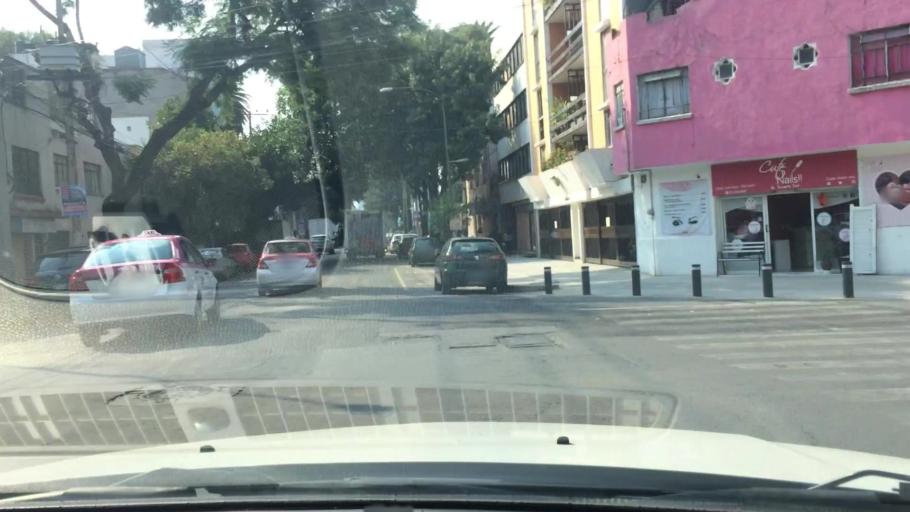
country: MX
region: Mexico City
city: Colonia del Valle
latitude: 19.3830
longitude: -99.1588
